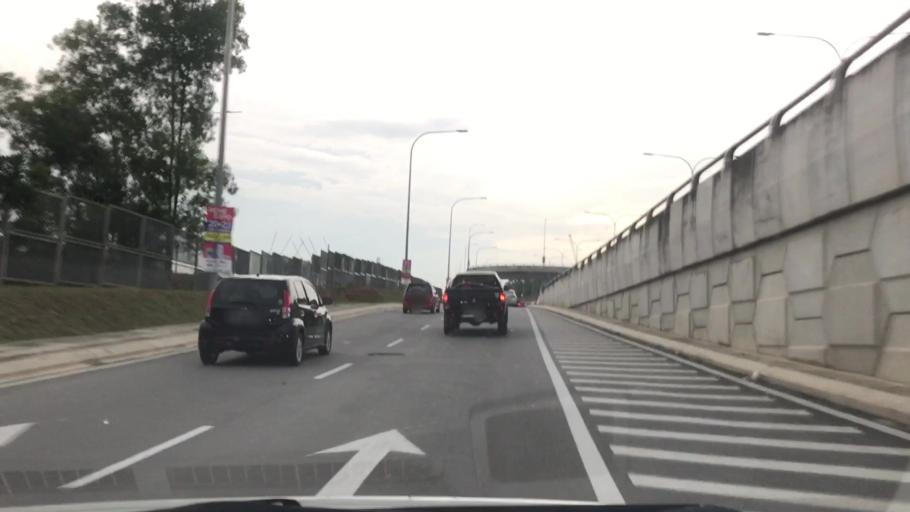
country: MY
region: Selangor
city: Kampong Baharu Balakong
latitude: 3.0490
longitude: 101.6788
